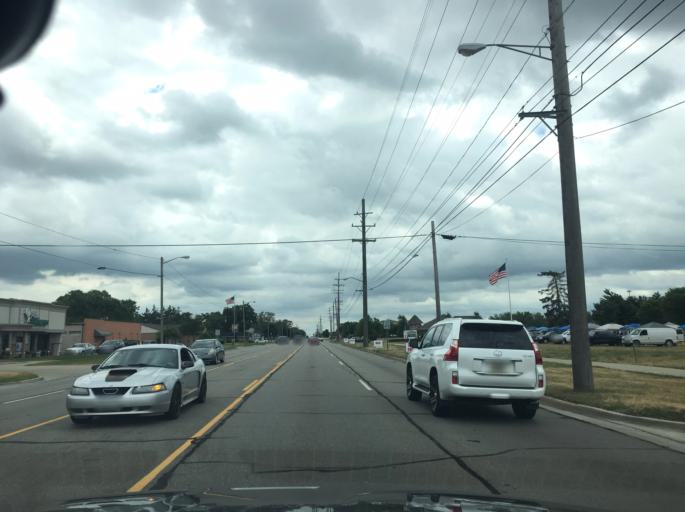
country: US
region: Michigan
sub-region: Macomb County
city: Shelby
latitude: 42.6626
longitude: -83.0337
